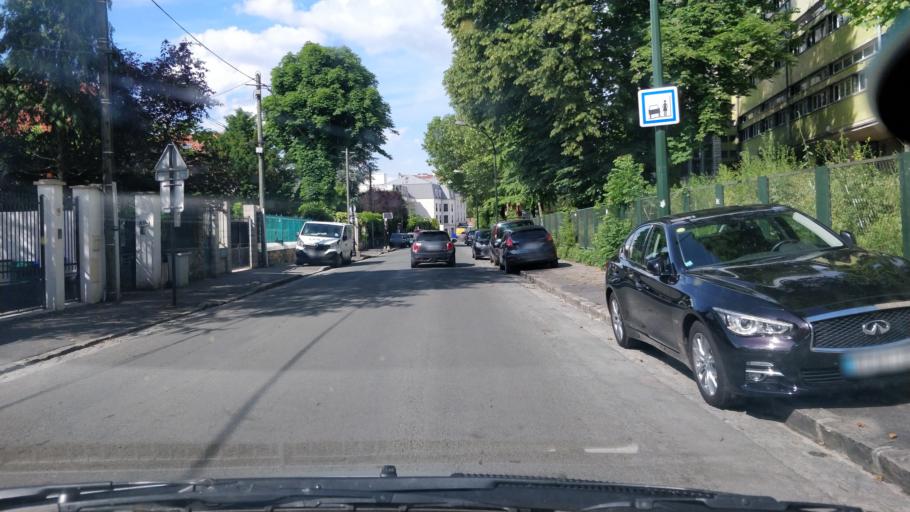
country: FR
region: Ile-de-France
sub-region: Departement de Seine-Saint-Denis
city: Le Raincy
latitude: 48.8997
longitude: 2.5108
